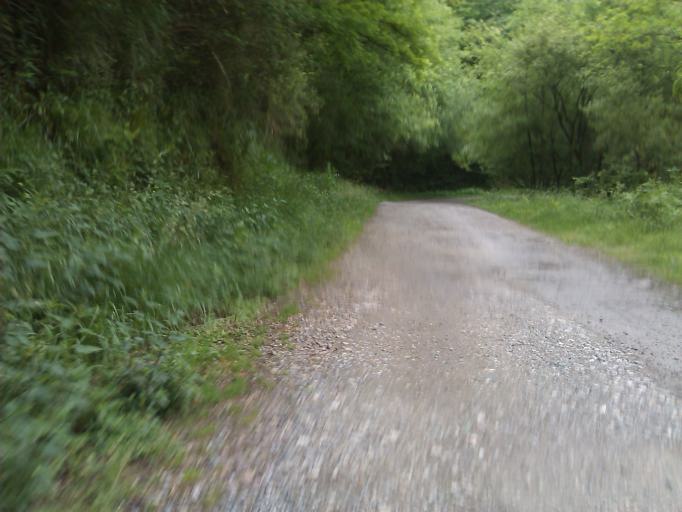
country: ES
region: Basque Country
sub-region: Provincia de Guipuzcoa
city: Andoain
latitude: 43.1874
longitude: -1.9965
